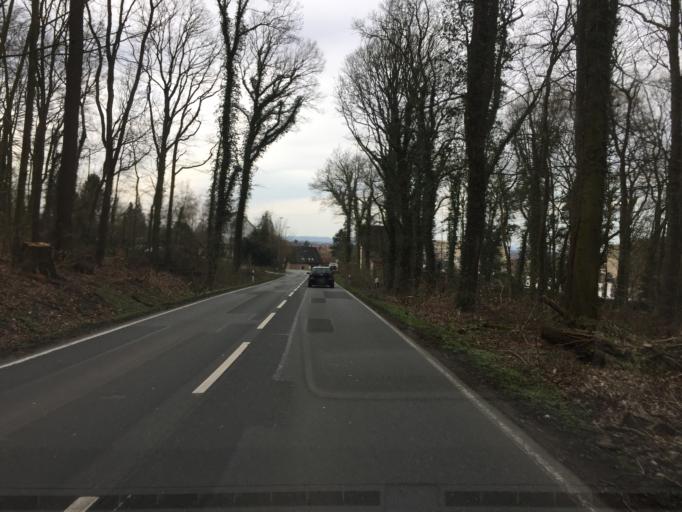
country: DE
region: North Rhine-Westphalia
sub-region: Regierungsbezirk Detmold
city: Bad Salzuflen
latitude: 52.0984
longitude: 8.7676
